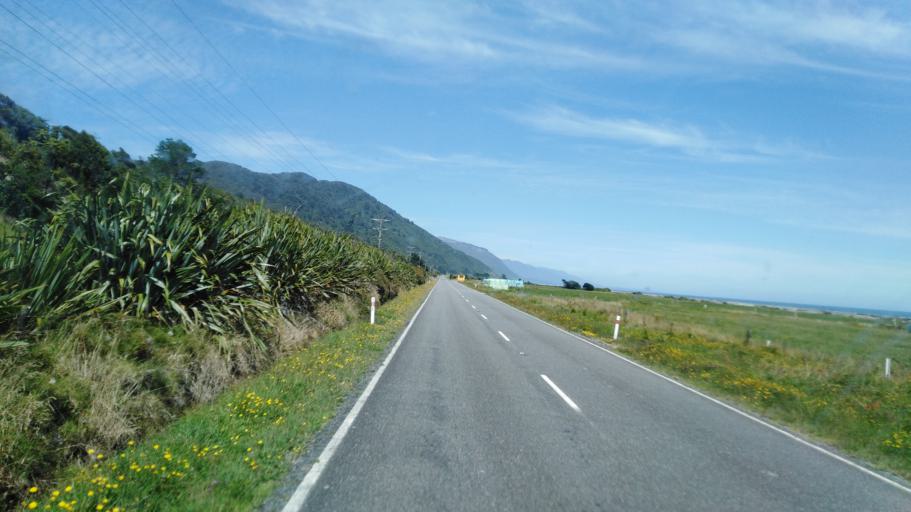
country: NZ
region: West Coast
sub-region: Buller District
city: Westport
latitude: -41.5437
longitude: 171.9267
